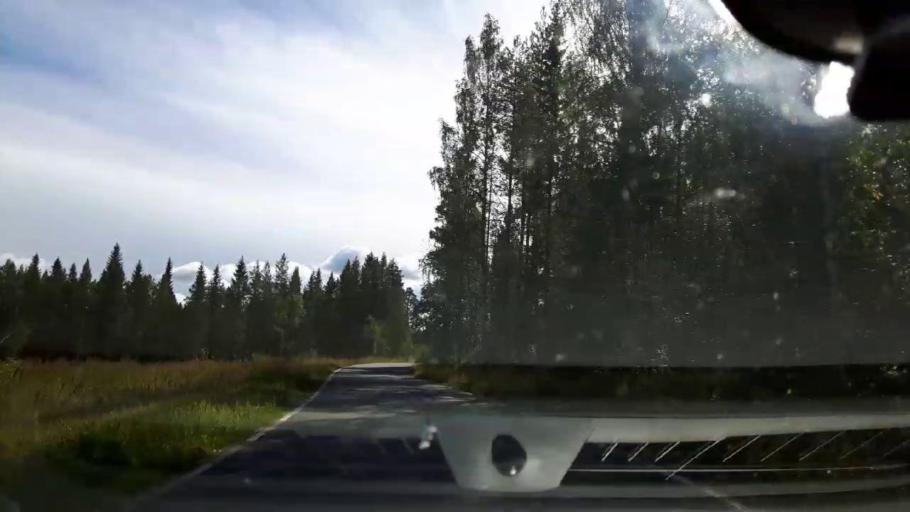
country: SE
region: Jaemtland
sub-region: Braecke Kommun
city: Braecke
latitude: 63.2063
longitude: 15.3528
